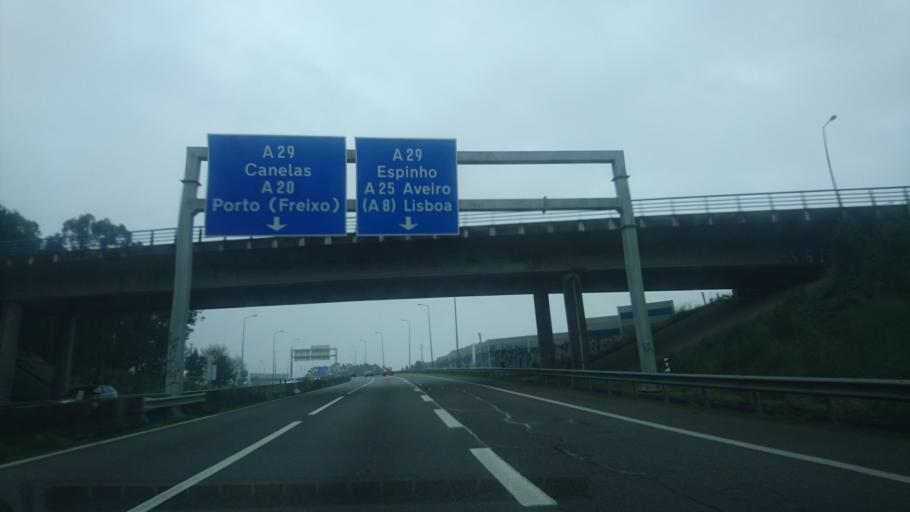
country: PT
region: Porto
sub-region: Vila Nova de Gaia
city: Gulpilhares
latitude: 41.0840
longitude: -8.6311
